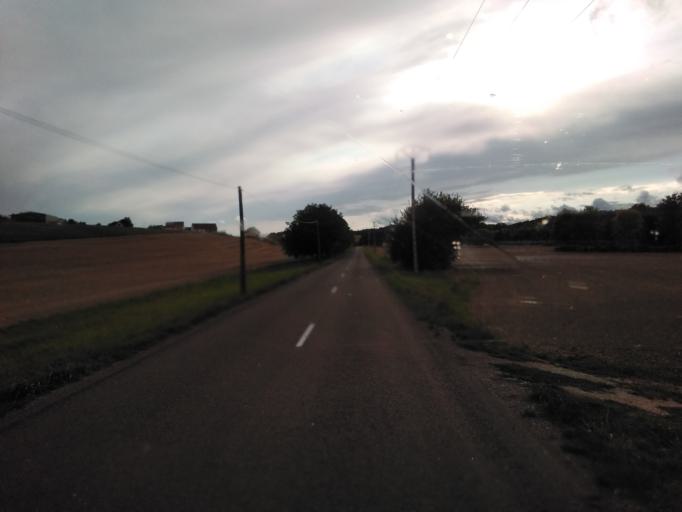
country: FR
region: Champagne-Ardenne
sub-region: Departement de l'Aube
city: Les Riceys
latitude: 47.9418
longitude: 4.3604
